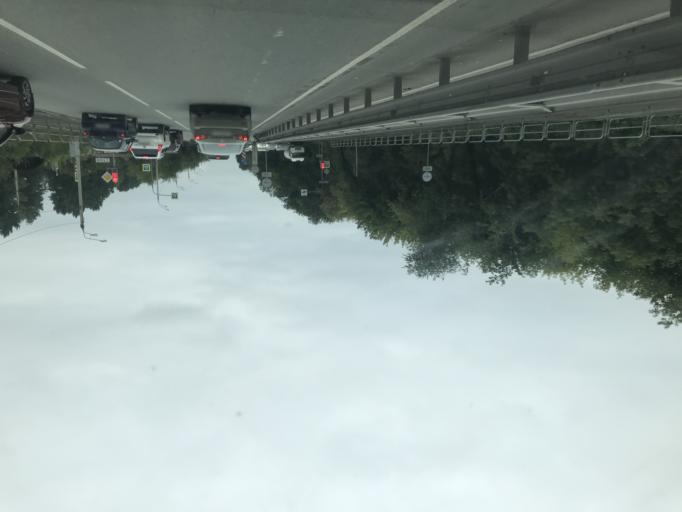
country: RU
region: Chelyabinsk
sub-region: Gorod Chelyabinsk
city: Chelyabinsk
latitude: 55.1792
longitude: 61.4206
